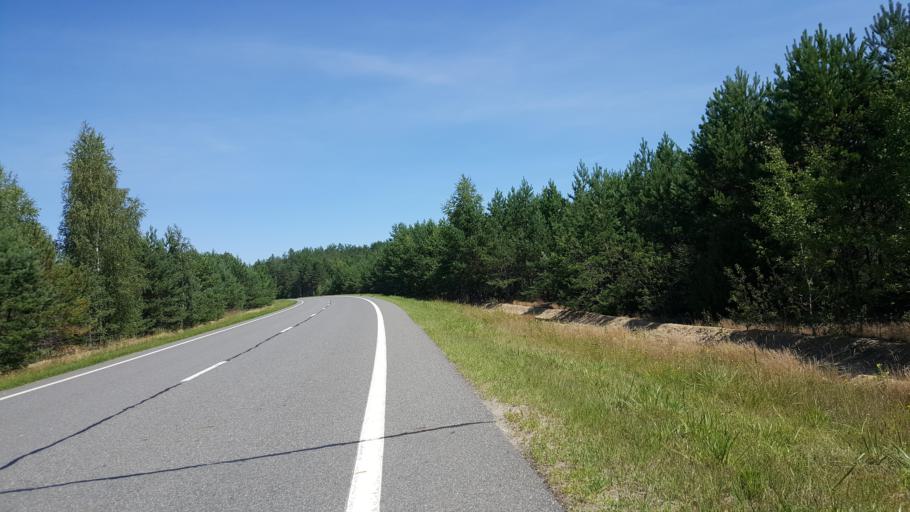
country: BY
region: Brest
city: Zhabinka
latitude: 52.4469
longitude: 24.1366
